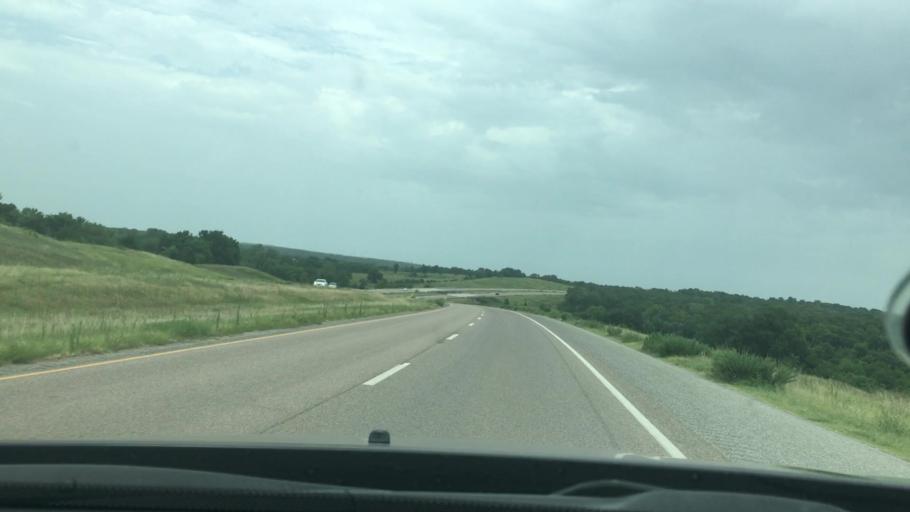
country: US
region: Oklahoma
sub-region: Pontotoc County
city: Ada
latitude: 34.8049
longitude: -96.6949
